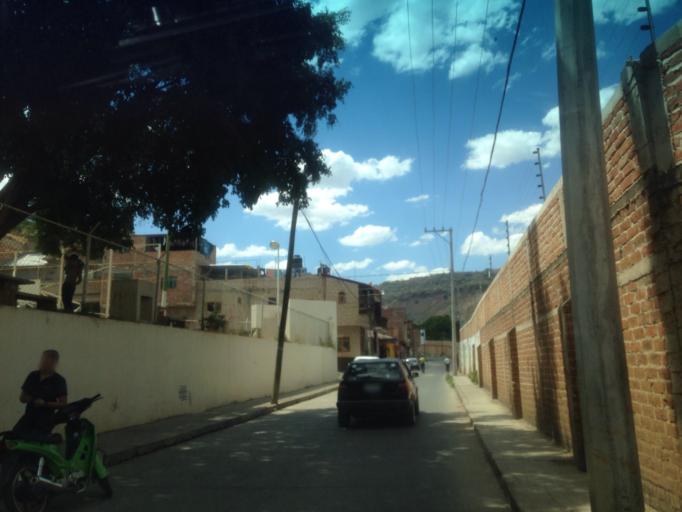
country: MX
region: Jalisco
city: Atotonilco el Alto
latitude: 20.5582
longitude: -102.5114
